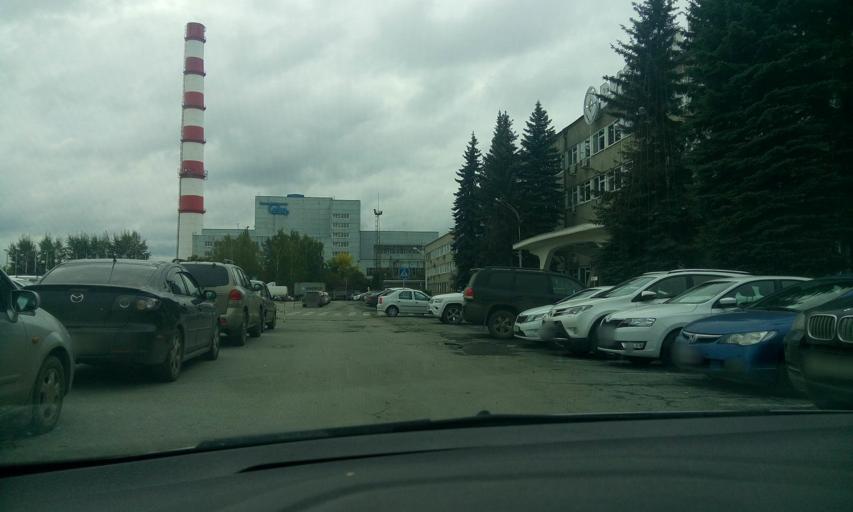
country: RU
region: Sverdlovsk
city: Yekaterinburg
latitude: 56.8520
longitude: 60.5467
